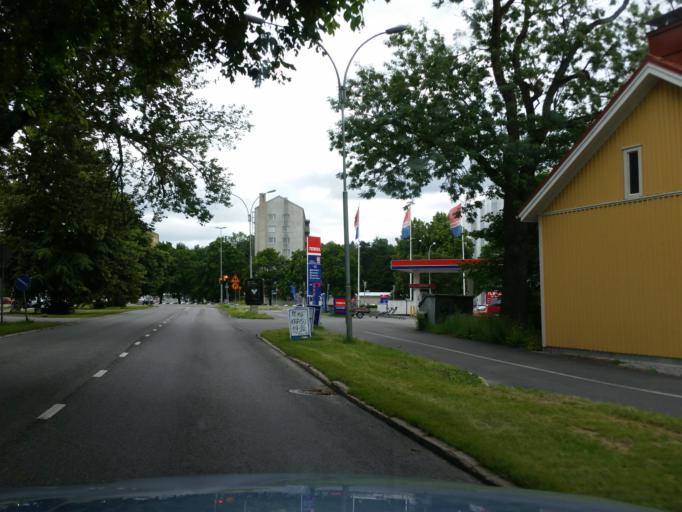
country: FI
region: Varsinais-Suomi
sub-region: Turku
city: Turku
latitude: 60.4381
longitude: 22.2913
